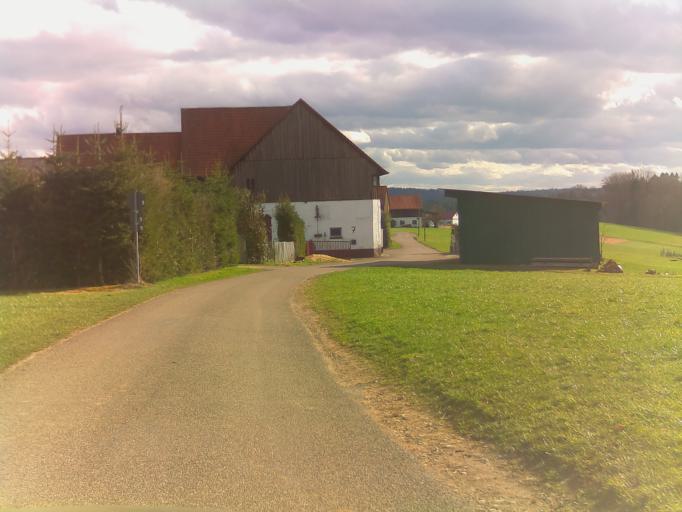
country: DE
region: Baden-Wuerttemberg
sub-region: Regierungsbezirk Stuttgart
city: Lorch
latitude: 48.8190
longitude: 9.6585
